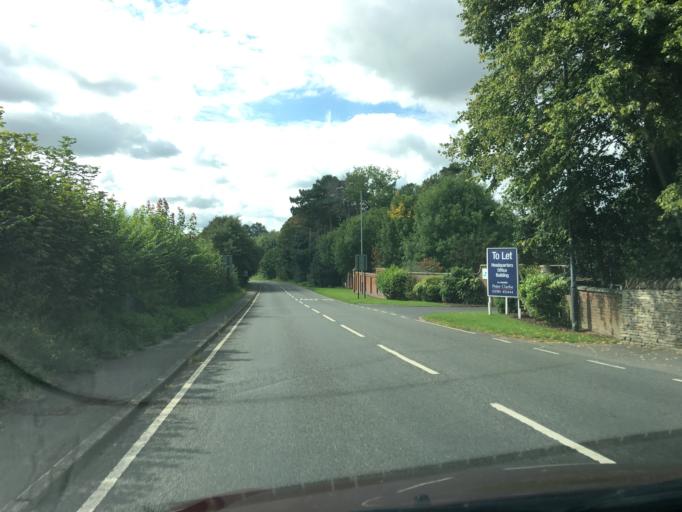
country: GB
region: England
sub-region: Warwickshire
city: Royal Leamington Spa
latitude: 52.3145
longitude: -1.5373
